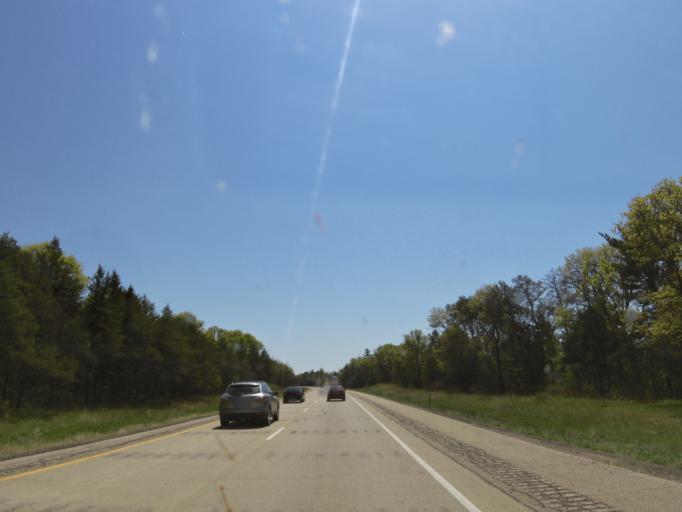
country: US
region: Wisconsin
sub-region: Monroe County
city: Tomah
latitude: 44.1771
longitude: -90.6074
